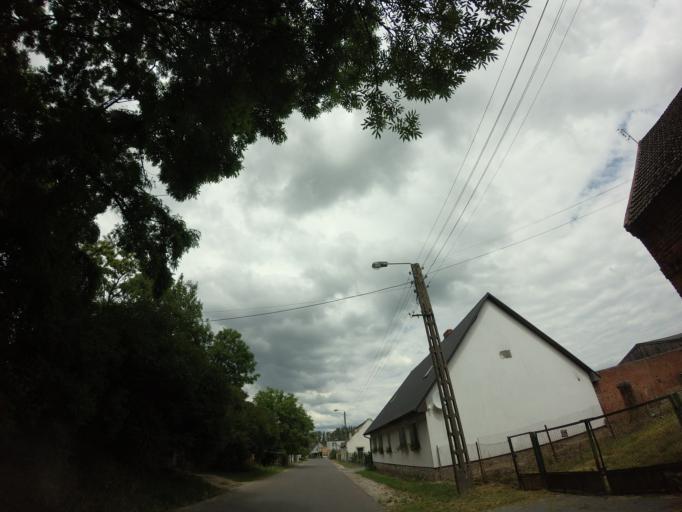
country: PL
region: West Pomeranian Voivodeship
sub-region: Powiat choszczenski
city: Choszczno
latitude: 53.1689
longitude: 15.4986
